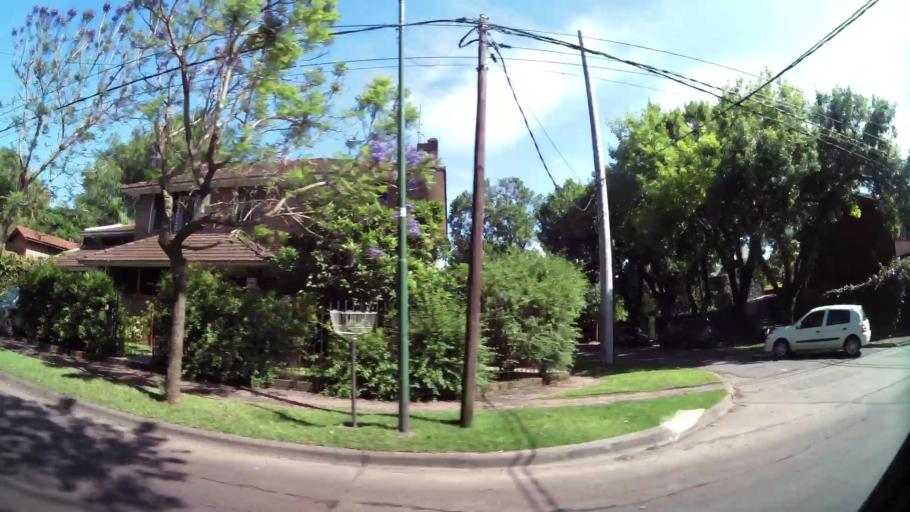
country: AR
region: Buenos Aires
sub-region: Partido de Tigre
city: Tigre
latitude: -34.4797
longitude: -58.5657
